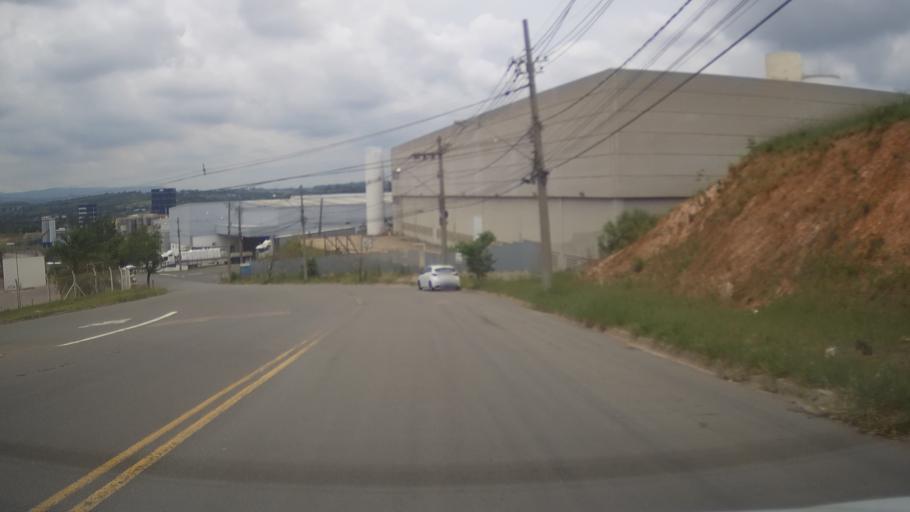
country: BR
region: Sao Paulo
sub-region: Itupeva
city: Itupeva
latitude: -23.1555
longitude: -47.0127
